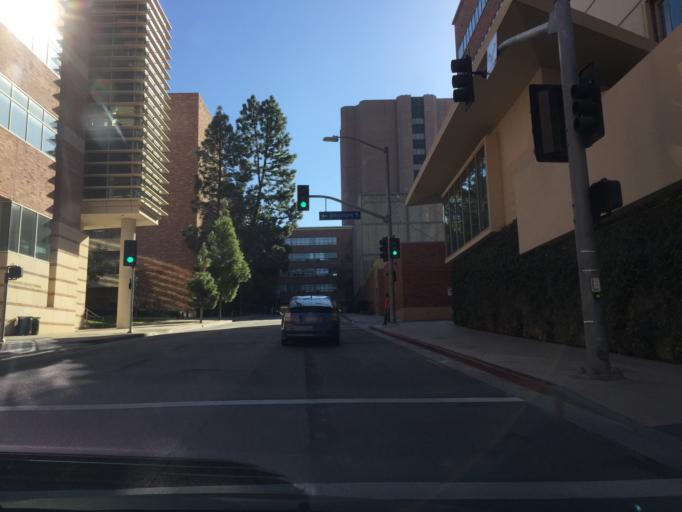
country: US
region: California
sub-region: Los Angeles County
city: Westwood, Los Angeles
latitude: 34.0670
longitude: -118.4441
